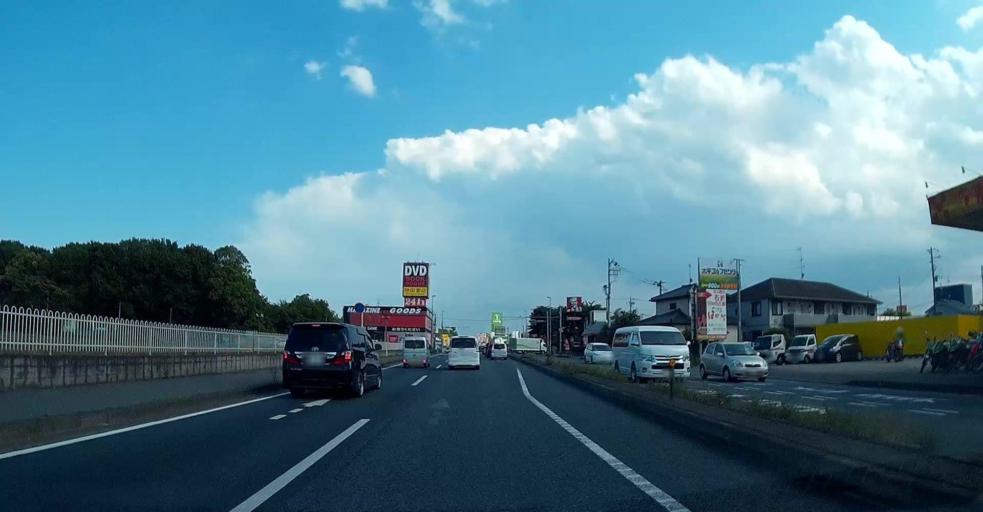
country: JP
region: Chiba
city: Noda
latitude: 35.9445
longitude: 139.8849
